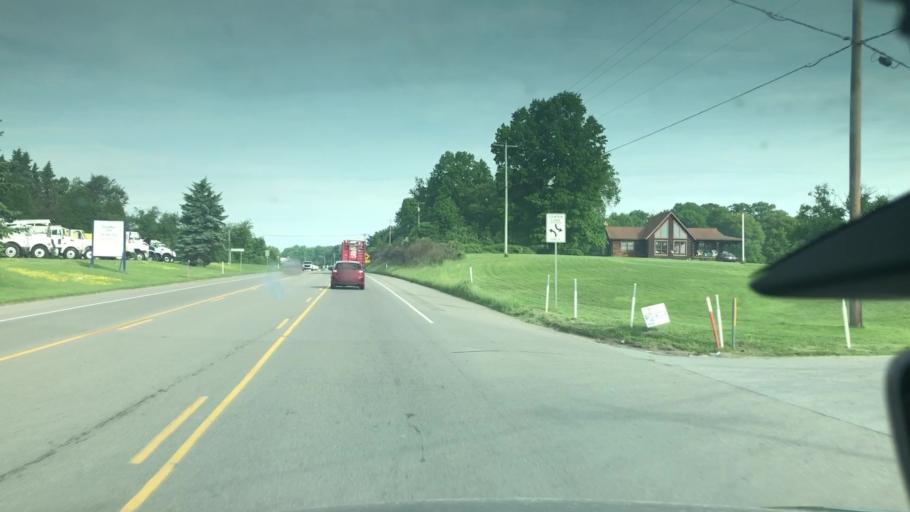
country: US
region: Pennsylvania
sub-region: Butler County
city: Prospect
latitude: 40.9031
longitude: -80.0163
